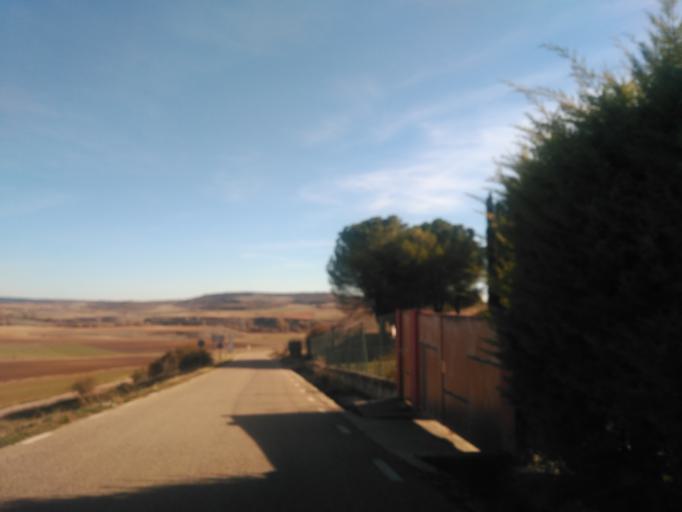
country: ES
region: Castille and Leon
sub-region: Provincia de Burgos
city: Coruna del Conde
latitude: 41.7869
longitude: -3.3659
